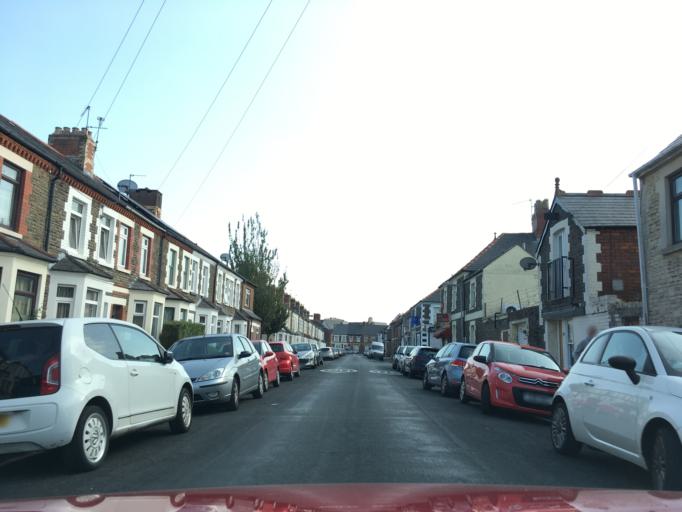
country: GB
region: Wales
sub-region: Cardiff
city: Cardiff
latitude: 51.4921
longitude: -3.1642
